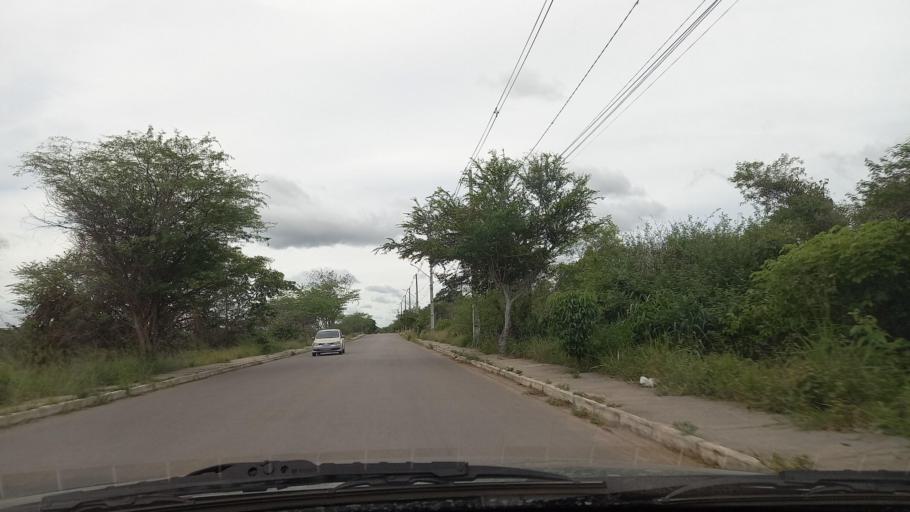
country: BR
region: Pernambuco
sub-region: Gravata
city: Gravata
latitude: -8.2097
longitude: -35.5961
